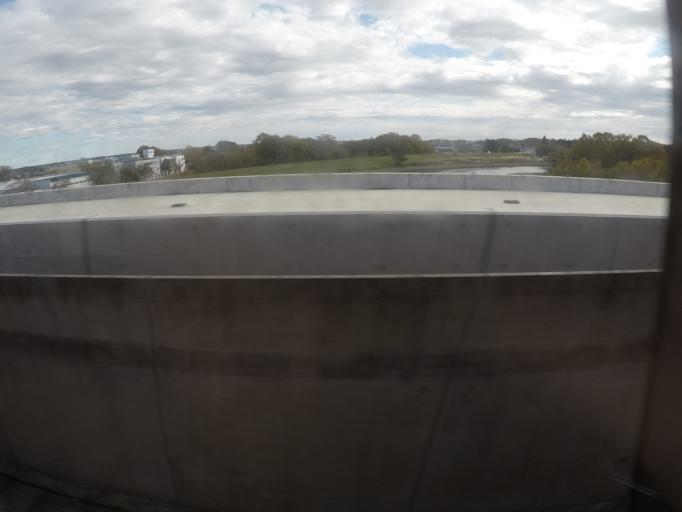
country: JP
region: Ibaraki
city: Moriya
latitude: 35.9630
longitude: 140.0056
